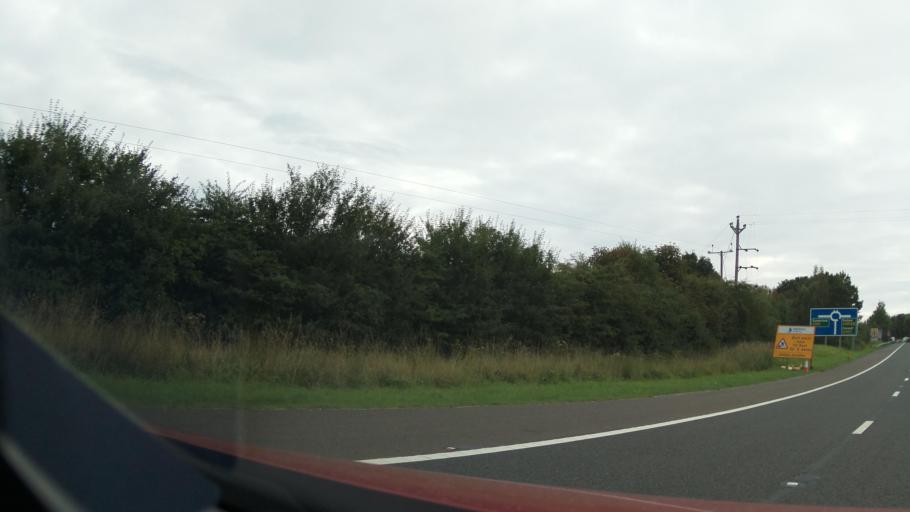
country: GB
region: England
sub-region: County Durham
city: West Rainton
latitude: 54.7968
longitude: -1.5263
